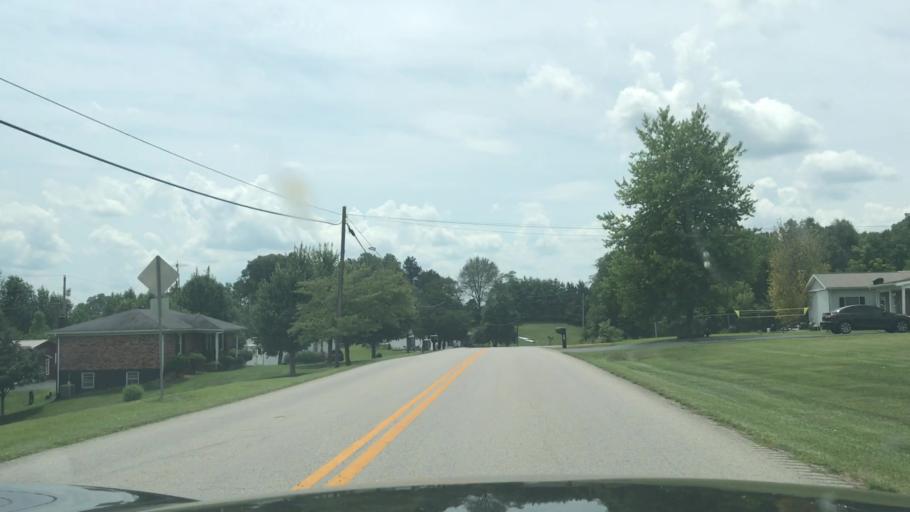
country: US
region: Kentucky
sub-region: Green County
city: Greensburg
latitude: 37.2794
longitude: -85.5220
